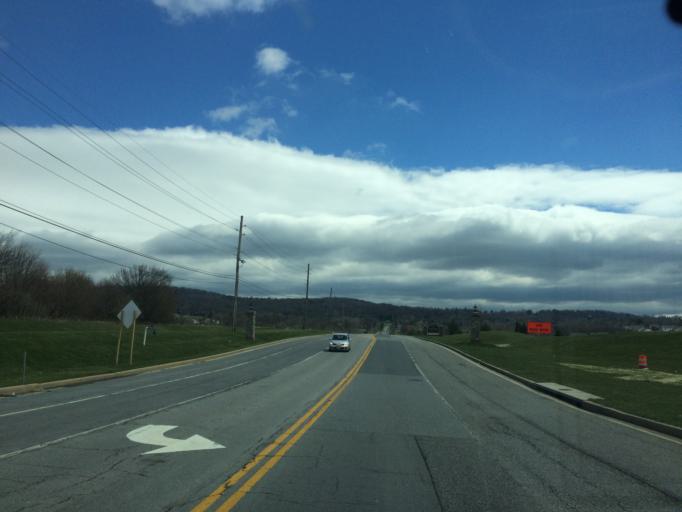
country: US
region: Maryland
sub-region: Frederick County
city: Middletown
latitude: 39.4376
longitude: -77.5268
